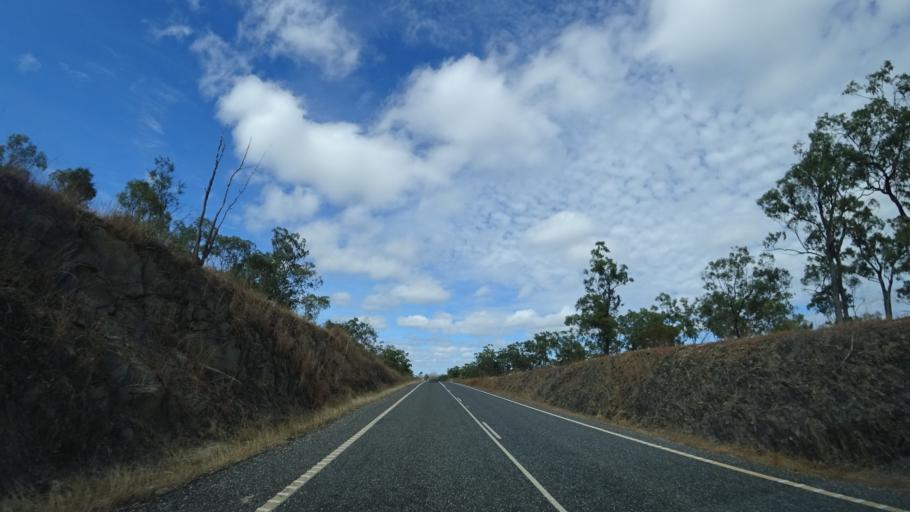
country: AU
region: Queensland
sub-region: Cairns
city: Port Douglas
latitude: -16.3158
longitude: 144.7183
